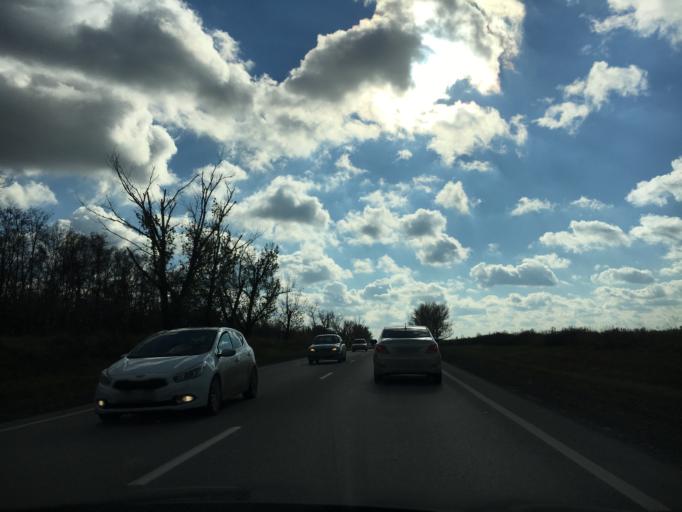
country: RU
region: Rostov
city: Matveyev Kurgan
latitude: 47.5274
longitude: 38.8952
